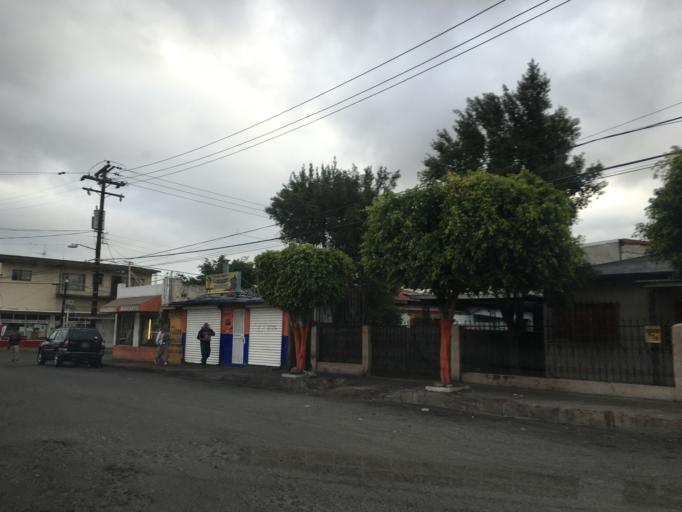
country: MX
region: Baja California
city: Tijuana
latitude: 32.5364
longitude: -117.0512
